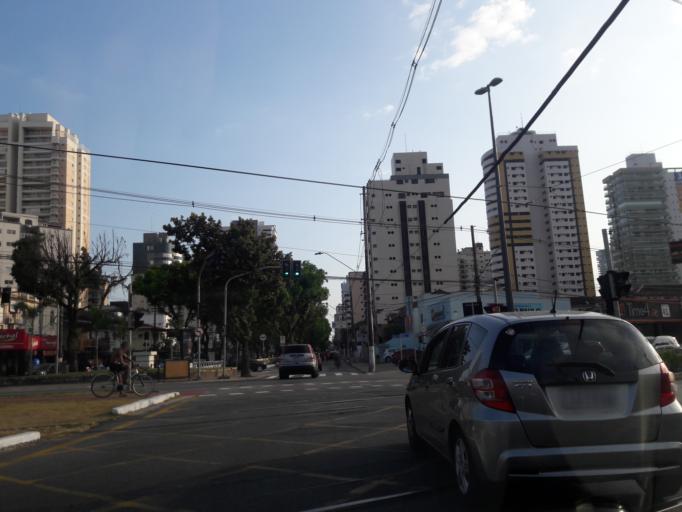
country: BR
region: Sao Paulo
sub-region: Santos
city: Santos
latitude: -23.9614
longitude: -46.3384
